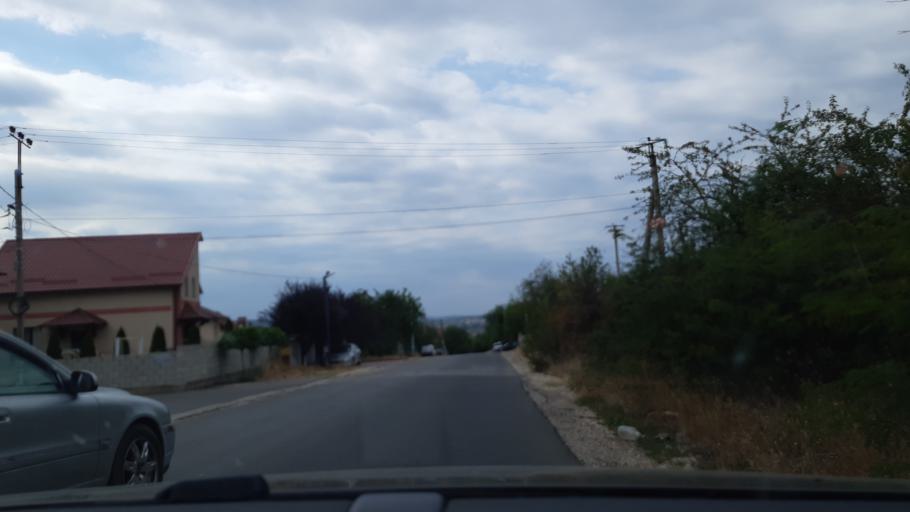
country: MD
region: Chisinau
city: Vatra
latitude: 47.0480
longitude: 28.7402
